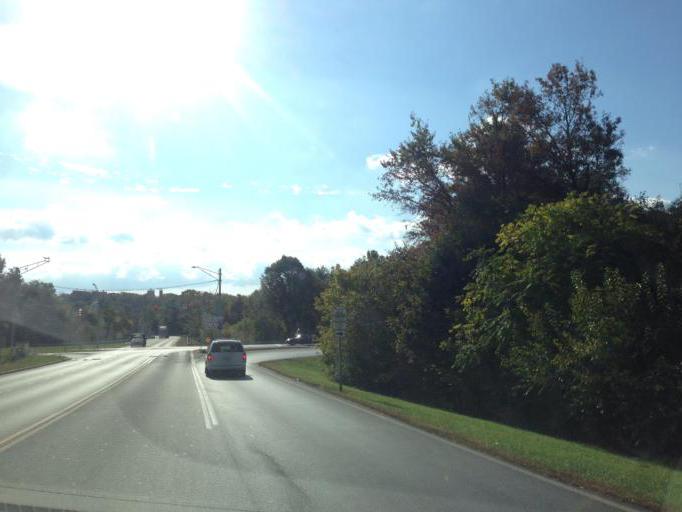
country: US
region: Maryland
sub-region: Carroll County
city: Mount Airy
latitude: 39.3626
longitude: -77.1647
